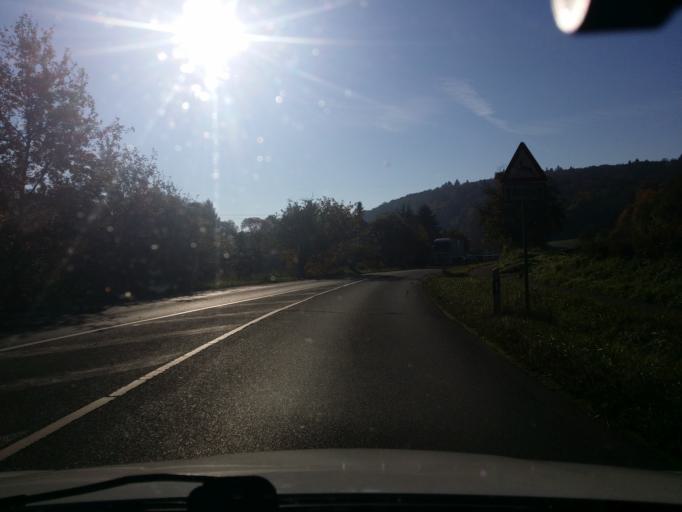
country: DE
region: Hesse
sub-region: Regierungsbezirk Darmstadt
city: Niedernhausen
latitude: 50.1579
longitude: 8.3217
